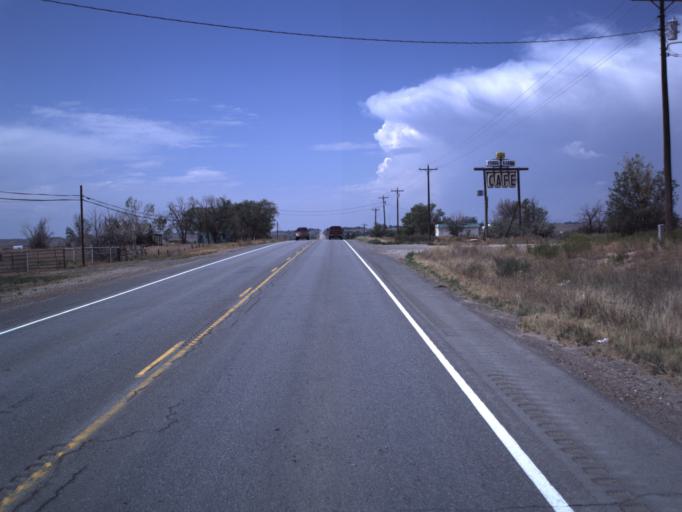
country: US
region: Utah
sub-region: Duchesne County
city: Roosevelt
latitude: 40.3020
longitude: -109.8317
